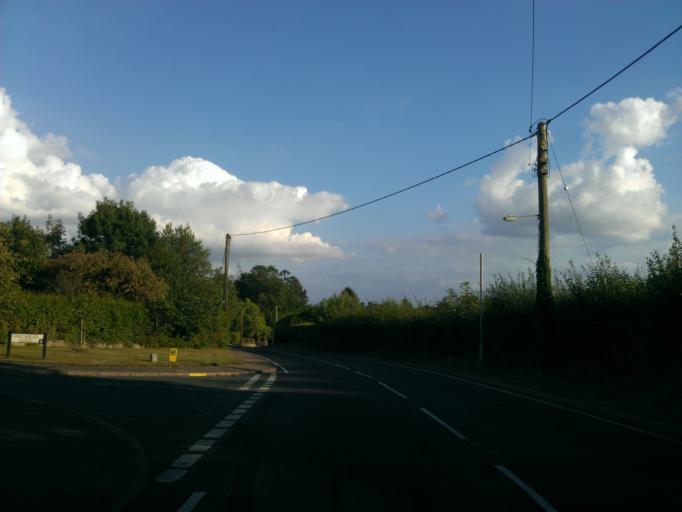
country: GB
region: England
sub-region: Essex
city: Sible Hedingham
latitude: 51.9342
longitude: 0.5934
